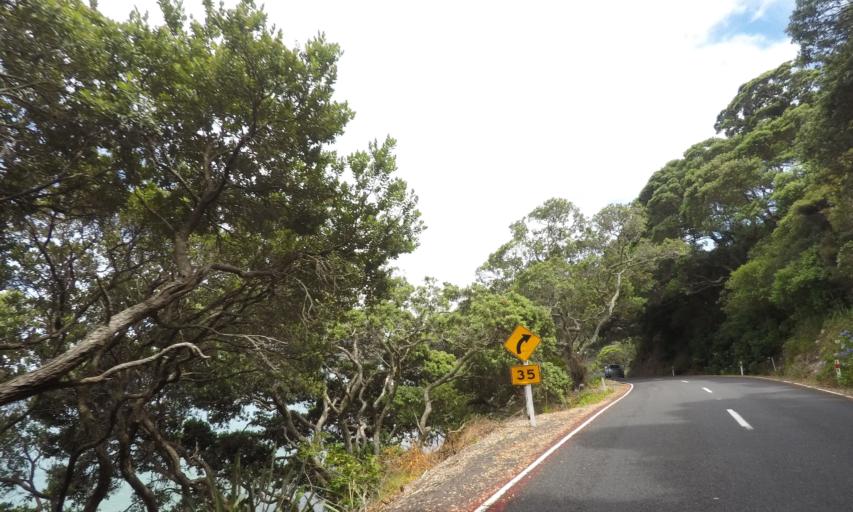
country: NZ
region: Northland
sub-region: Whangarei
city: Ruakaka
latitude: -35.8363
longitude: 174.5334
